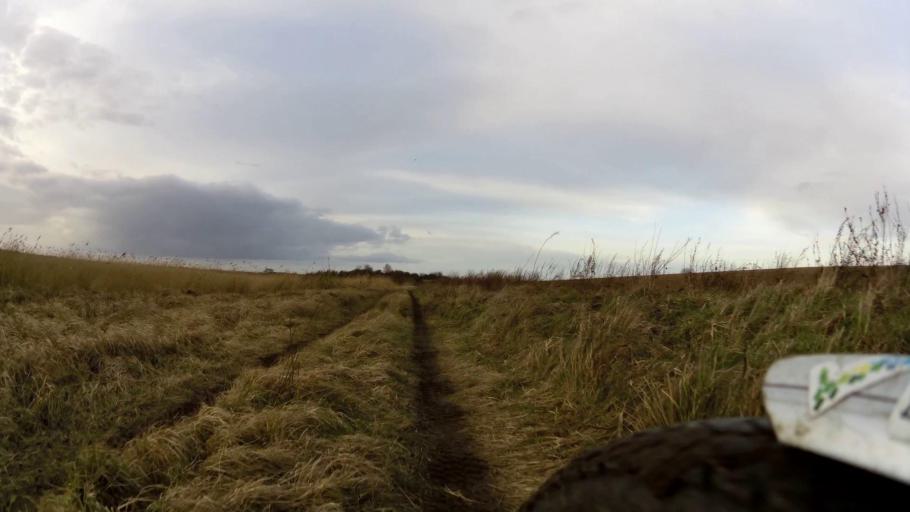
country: PL
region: West Pomeranian Voivodeship
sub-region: Powiat kamienski
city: Kamien Pomorski
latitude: 53.9290
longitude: 14.7626
